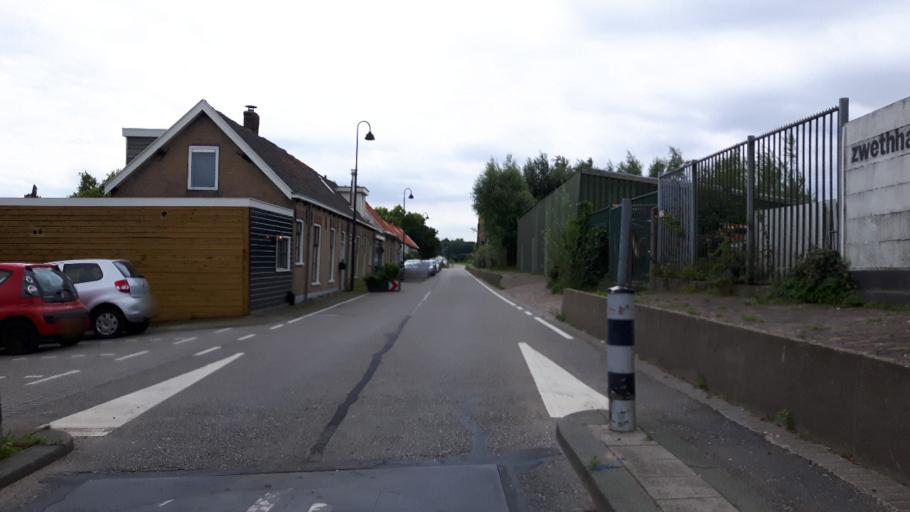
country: NL
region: South Holland
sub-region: Gemeente Schiedam
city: Schiedam
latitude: 51.9615
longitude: 4.3950
